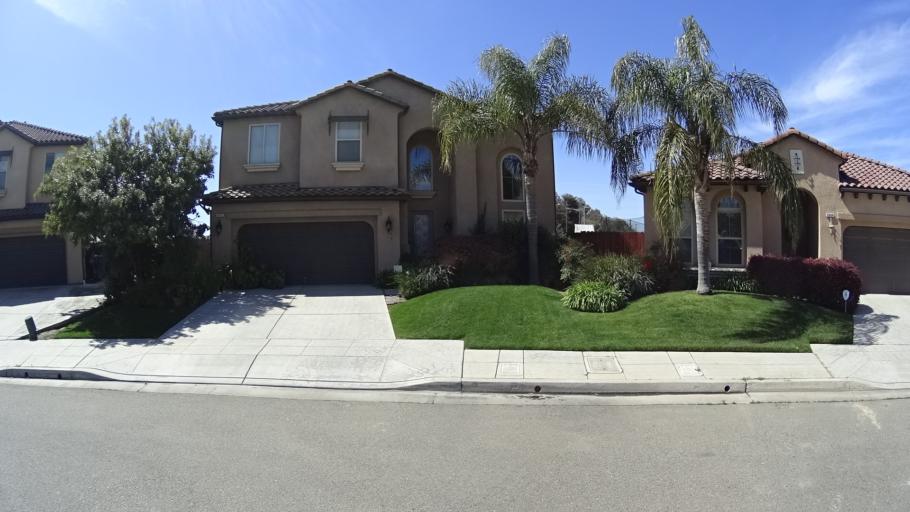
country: US
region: California
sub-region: Fresno County
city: Biola
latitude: 36.8157
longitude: -119.9153
